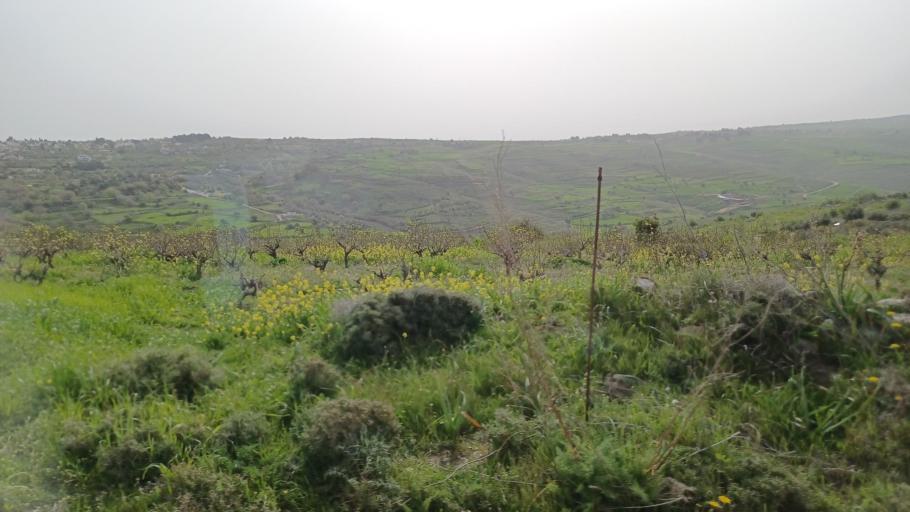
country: CY
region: Pafos
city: Pegeia
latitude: 34.9512
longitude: 32.3793
